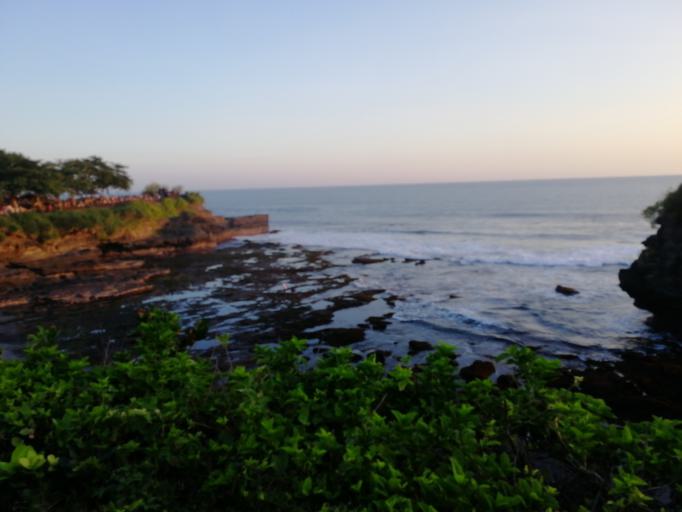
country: ID
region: Bali
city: Banjar Pangkungtibah Selatan
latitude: -8.6182
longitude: 115.0864
